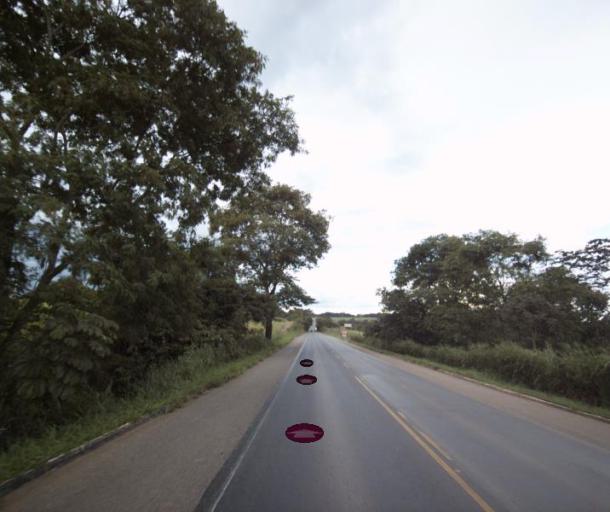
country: BR
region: Goias
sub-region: Itapaci
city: Itapaci
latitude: -15.0349
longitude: -49.4356
